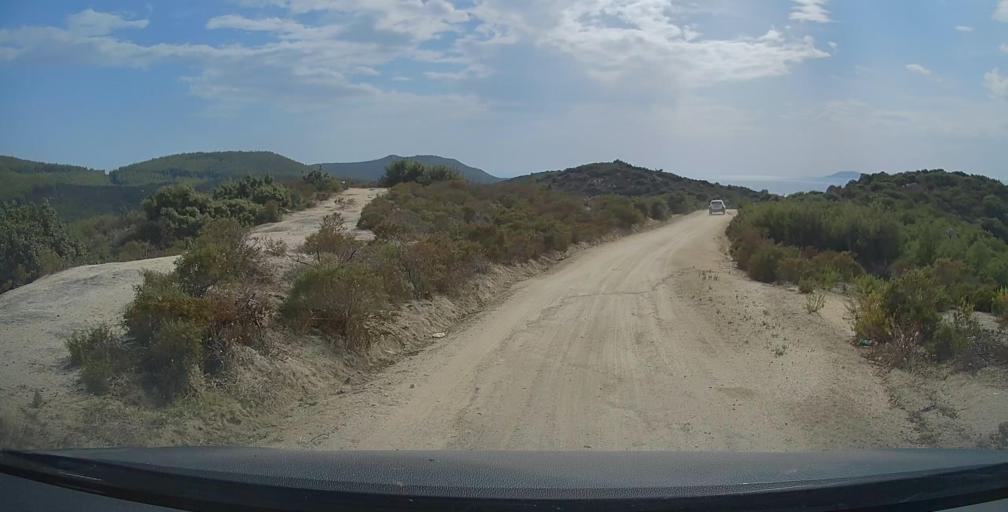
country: GR
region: Central Macedonia
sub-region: Nomos Chalkidikis
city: Sykia
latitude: 39.9960
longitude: 23.9224
